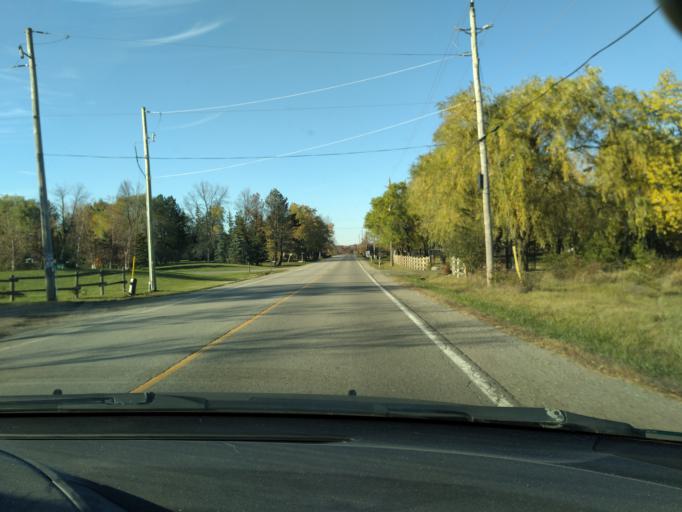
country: CA
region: Ontario
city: Vaughan
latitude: 43.8972
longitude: -79.7022
